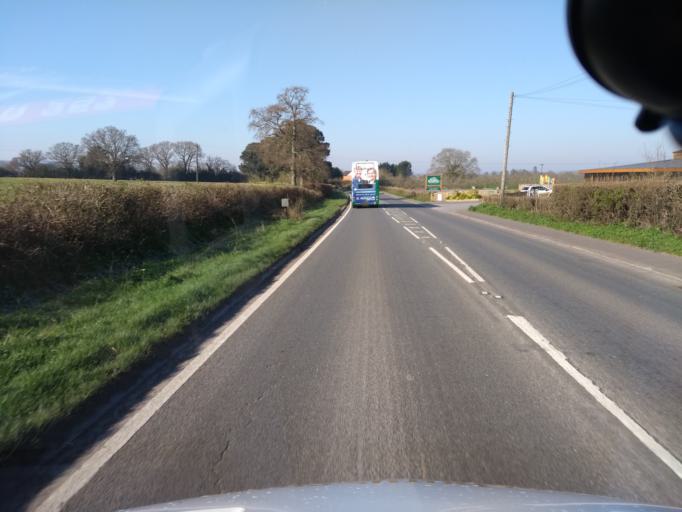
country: GB
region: England
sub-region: Somerset
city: Taunton
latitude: 51.0013
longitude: -3.1560
